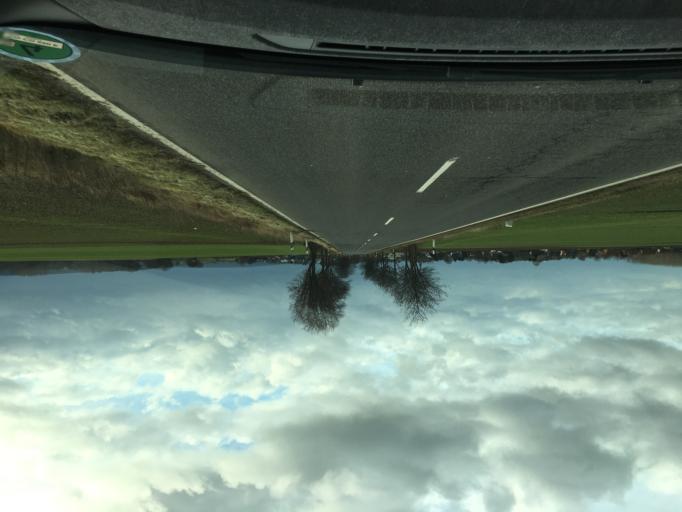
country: DE
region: North Rhine-Westphalia
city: Zulpich
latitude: 50.6745
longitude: 6.7029
